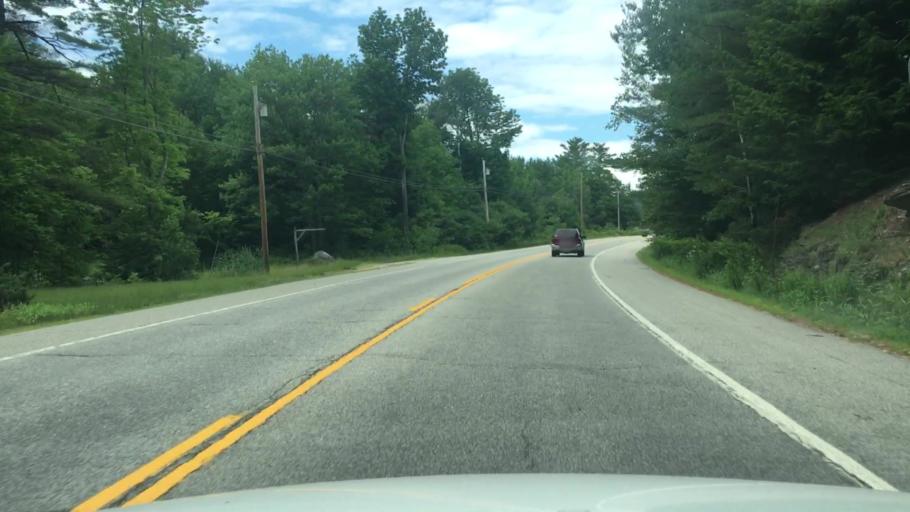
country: US
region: Maine
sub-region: Oxford County
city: West Paris
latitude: 44.3435
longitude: -70.5622
